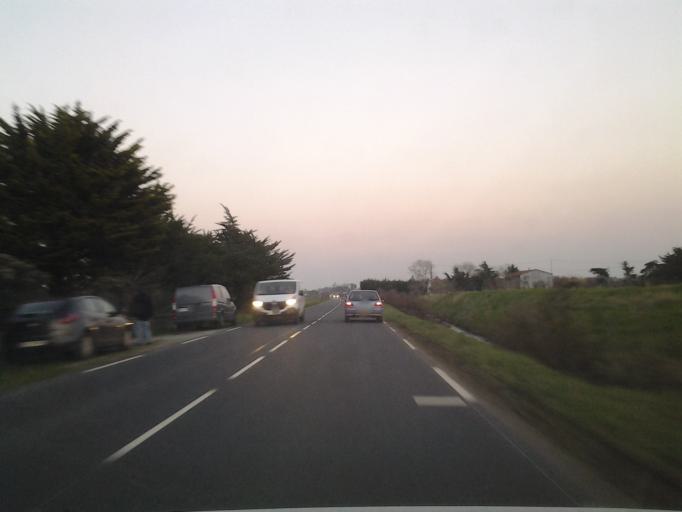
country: FR
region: Pays de la Loire
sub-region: Departement de la Vendee
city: Beauvoir-sur-Mer
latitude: 46.9155
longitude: -2.0591
